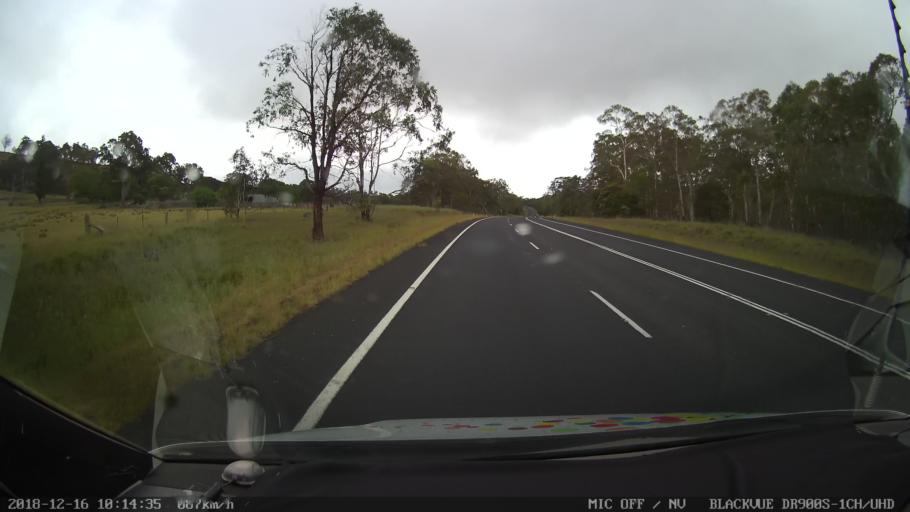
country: AU
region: New South Wales
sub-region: Tenterfield Municipality
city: Carrolls Creek
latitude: -29.2852
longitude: 151.9637
